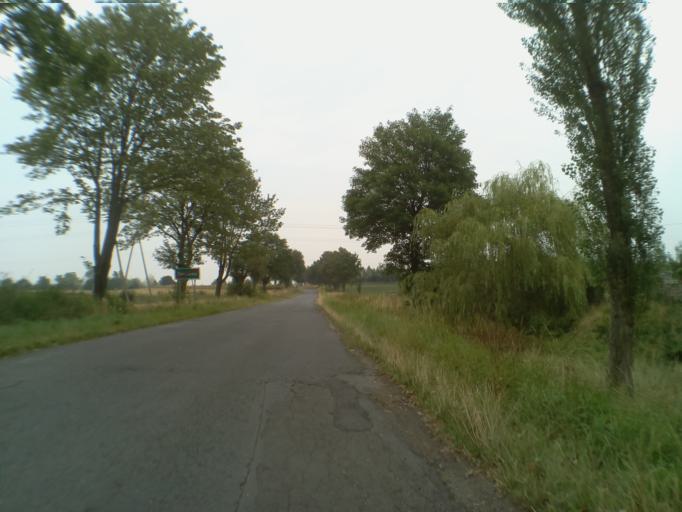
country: PL
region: Lower Silesian Voivodeship
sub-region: Powiat swidnicki
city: Strzegom
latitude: 50.9412
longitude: 16.3291
